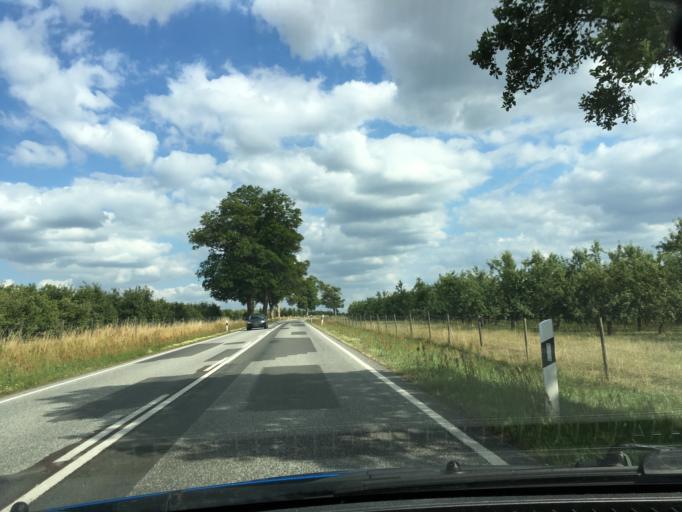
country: DE
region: Mecklenburg-Vorpommern
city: Lubtheen
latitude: 53.3869
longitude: 11.0664
